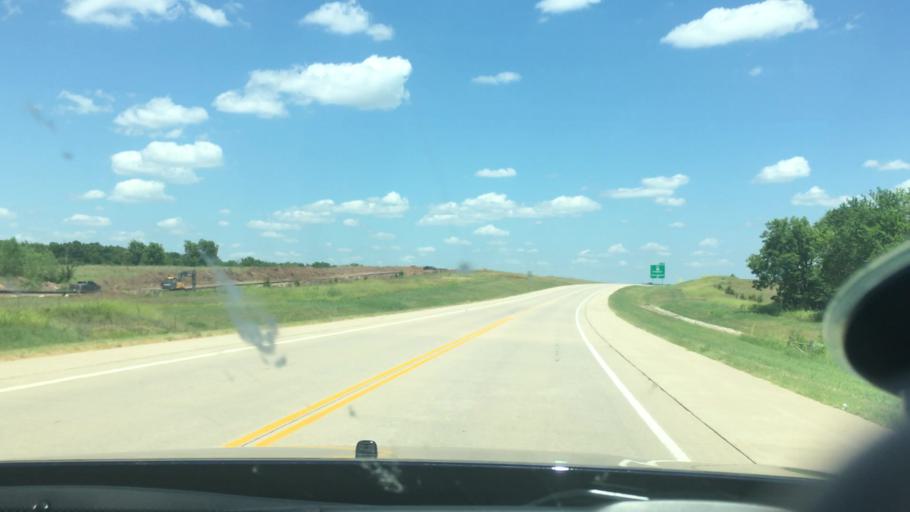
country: US
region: Oklahoma
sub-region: Murray County
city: Sulphur
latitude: 34.5438
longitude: -96.9791
